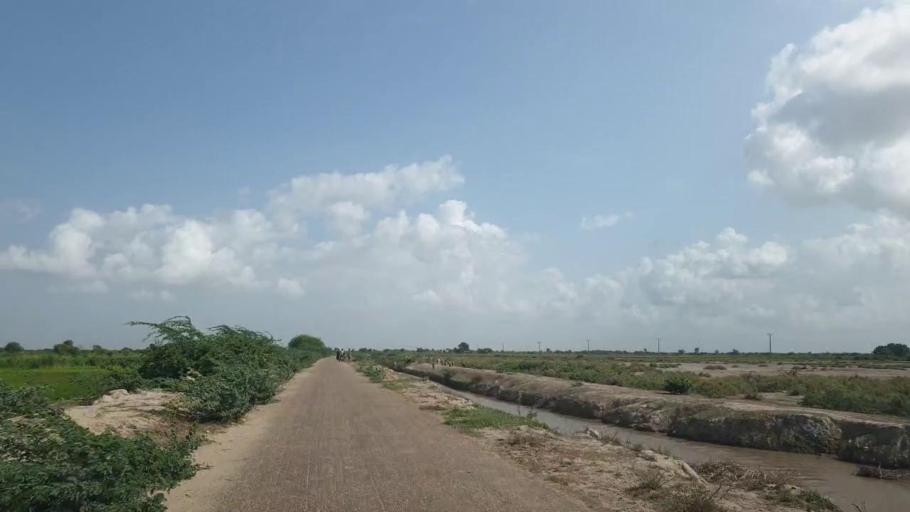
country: PK
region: Sindh
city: Kadhan
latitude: 24.5729
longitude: 69.0672
